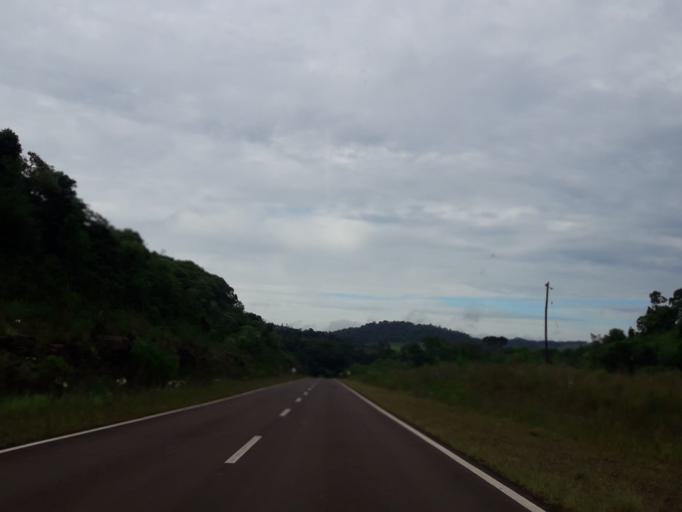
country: AR
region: Misiones
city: Bernardo de Irigoyen
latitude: -26.3258
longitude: -53.7576
